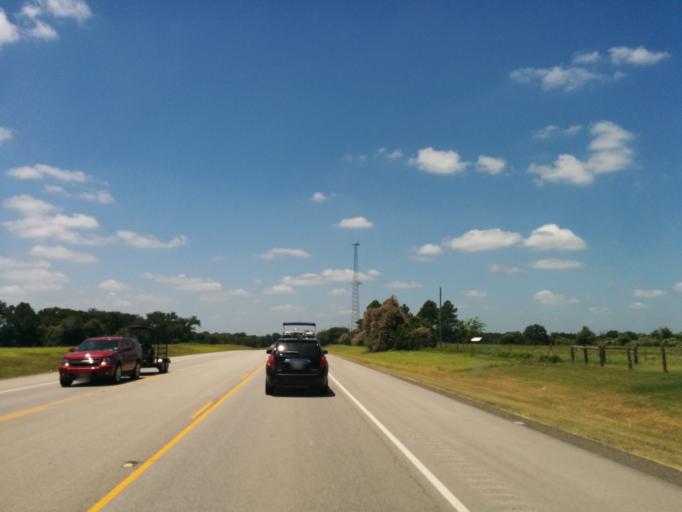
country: US
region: Texas
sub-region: Leon County
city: Hilltop Lakes
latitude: 30.8750
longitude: -96.1862
